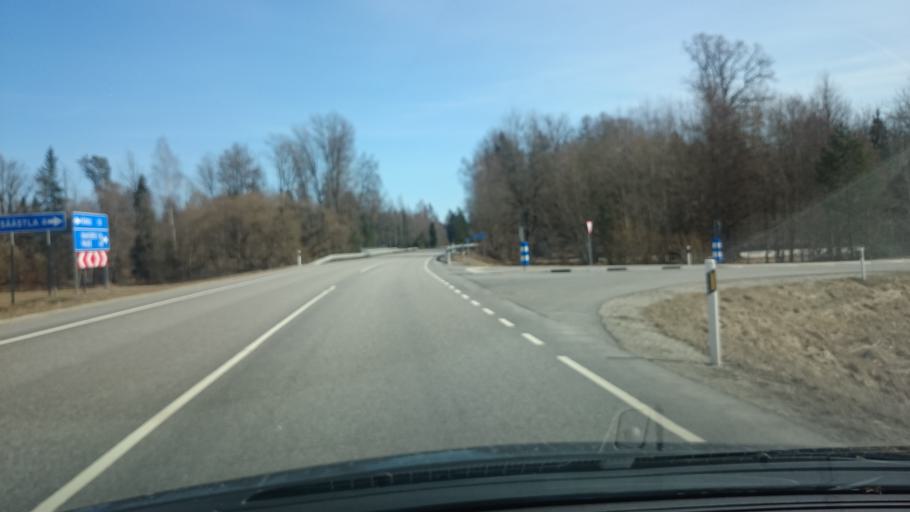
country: EE
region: Paernumaa
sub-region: Vaendra vald (alev)
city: Vandra
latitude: 58.6733
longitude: 25.1193
